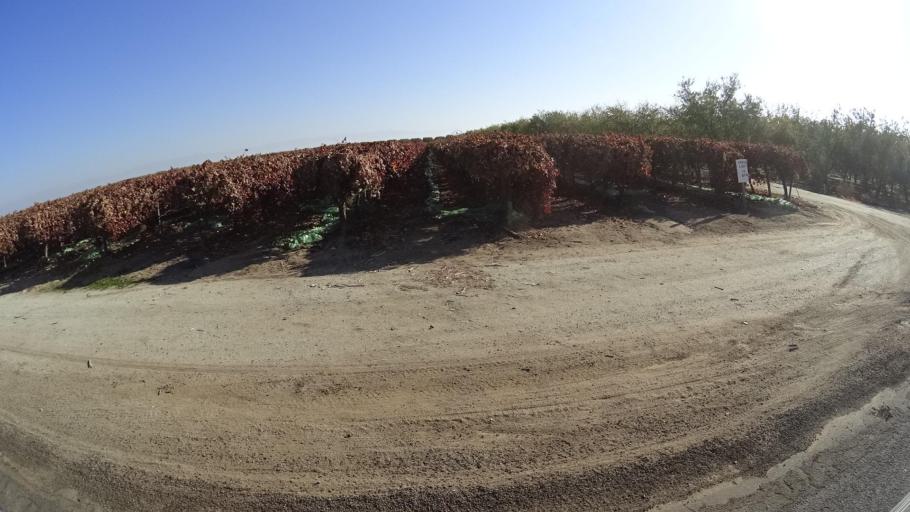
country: US
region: California
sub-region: Tulare County
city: Richgrove
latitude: 35.7399
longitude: -119.1341
